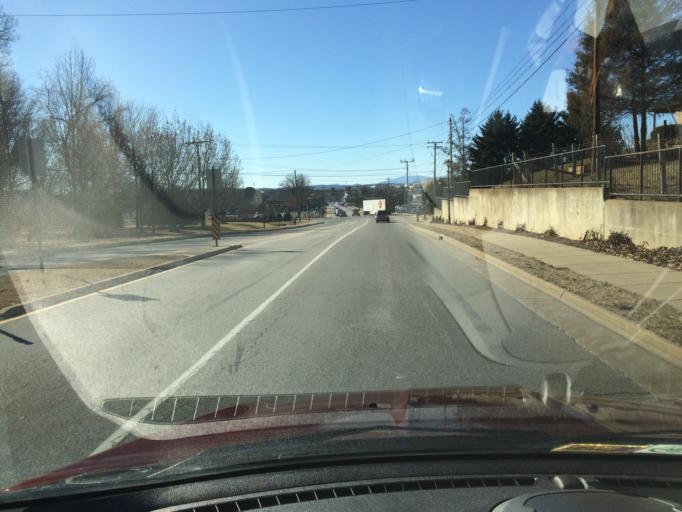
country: US
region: Virginia
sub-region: Rockingham County
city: Bridgewater
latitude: 38.3931
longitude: -78.9629
